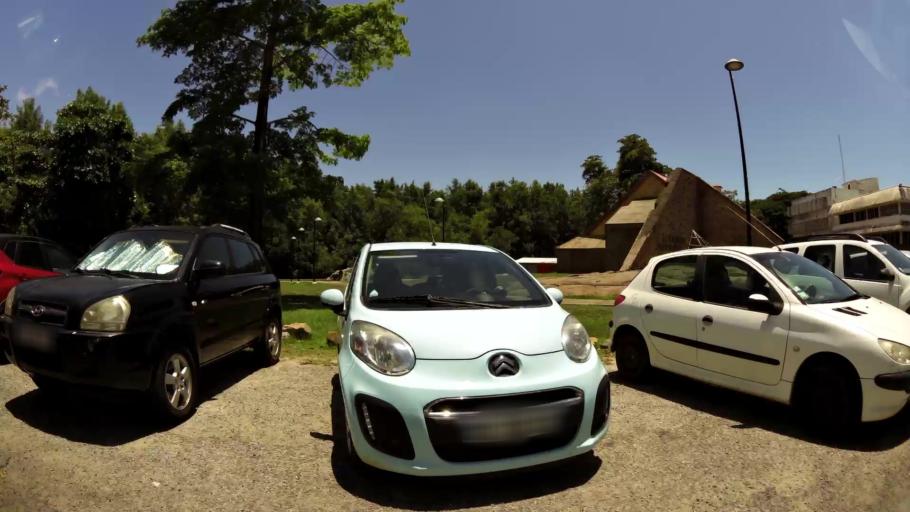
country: GF
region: Guyane
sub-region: Guyane
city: Cayenne
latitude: 4.9398
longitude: -52.3360
